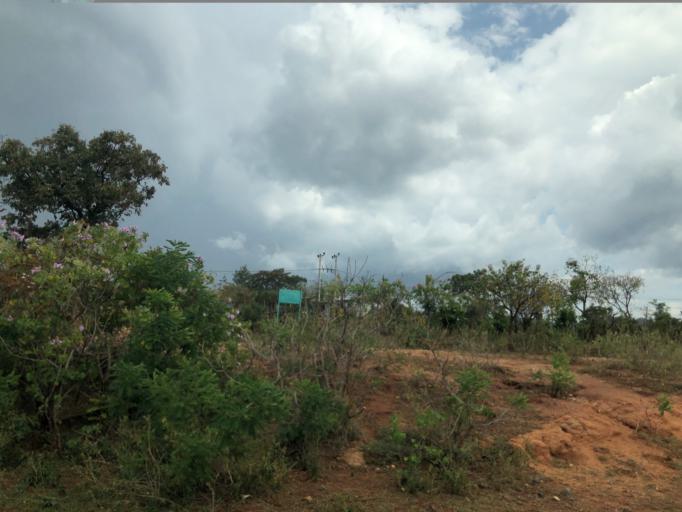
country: ET
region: Southern Nations, Nationalities, and People's Region
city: Jinka
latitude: 5.5978
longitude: 36.6932
